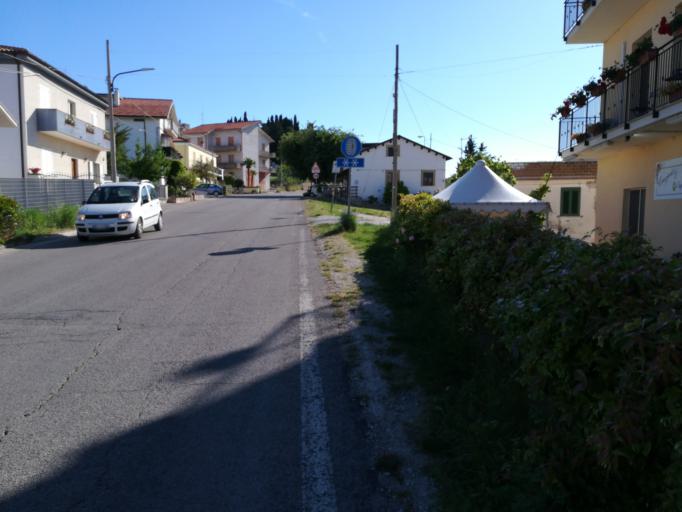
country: IT
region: Abruzzo
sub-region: Provincia di Chieti
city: Bucchianico
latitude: 42.2982
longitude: 14.1746
